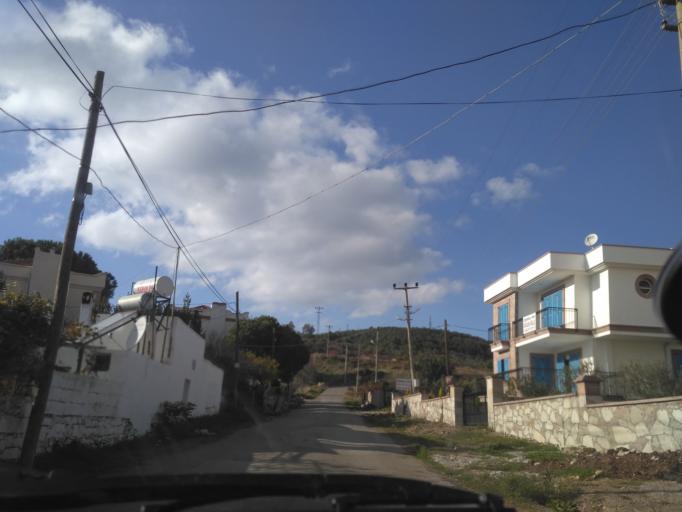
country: TR
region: Balikesir
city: Ayvalik
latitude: 39.3368
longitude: 26.6557
